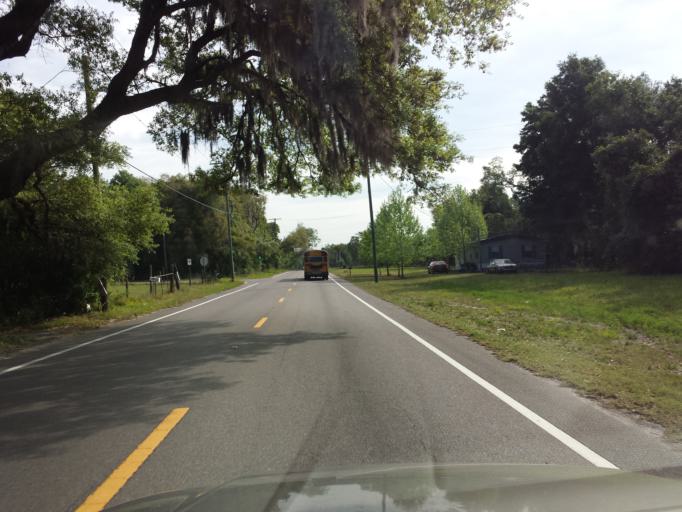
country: US
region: Florida
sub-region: Hillsborough County
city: Thonotosassa
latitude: 28.0379
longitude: -82.3418
